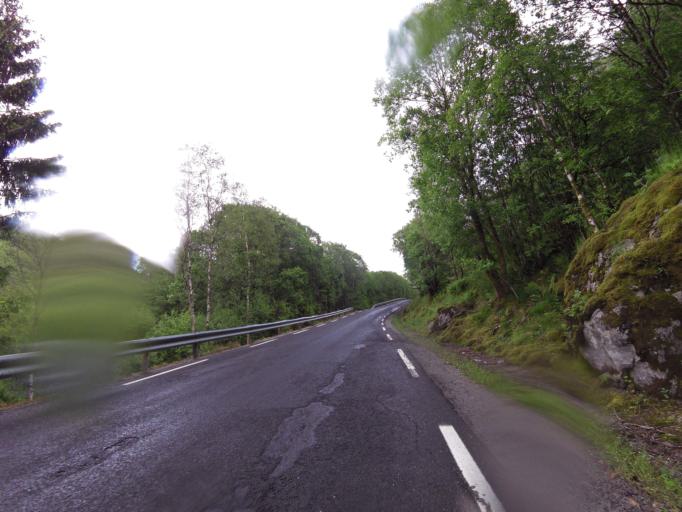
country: NO
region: Vest-Agder
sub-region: Lyngdal
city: Lyngdal
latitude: 58.1151
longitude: 7.0742
